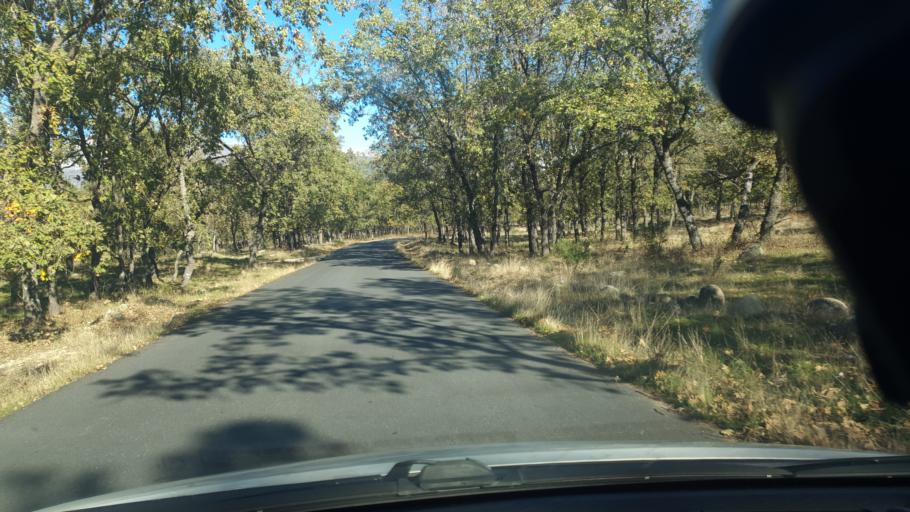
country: ES
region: Castille and Leon
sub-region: Provincia de Avila
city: Candeleda
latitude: 40.1286
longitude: -5.2666
